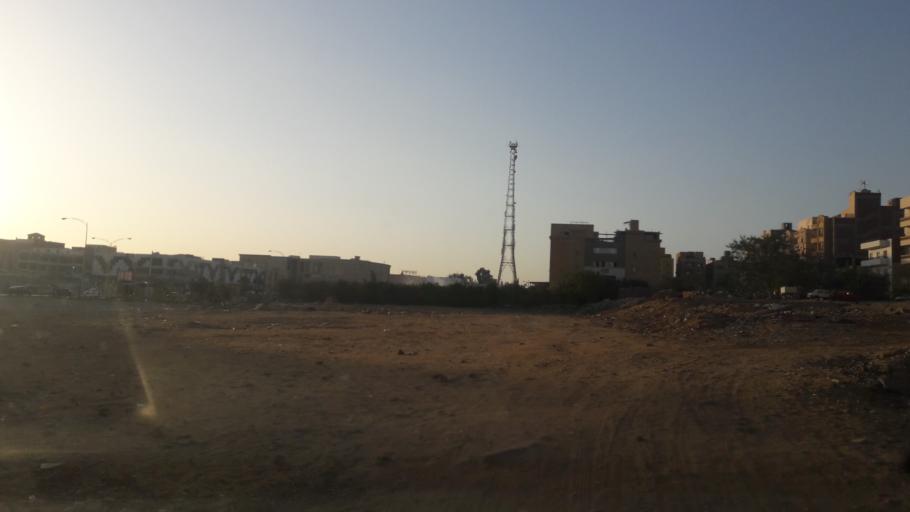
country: EG
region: Al Jizah
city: Madinat Sittah Uktubar
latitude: 29.9590
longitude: 30.9325
